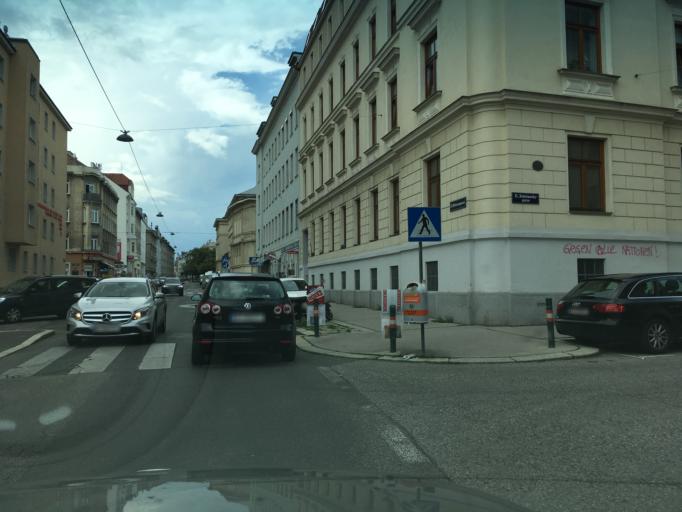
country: AT
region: Vienna
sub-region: Wien Stadt
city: Vienna
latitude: 48.2204
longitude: 16.3282
